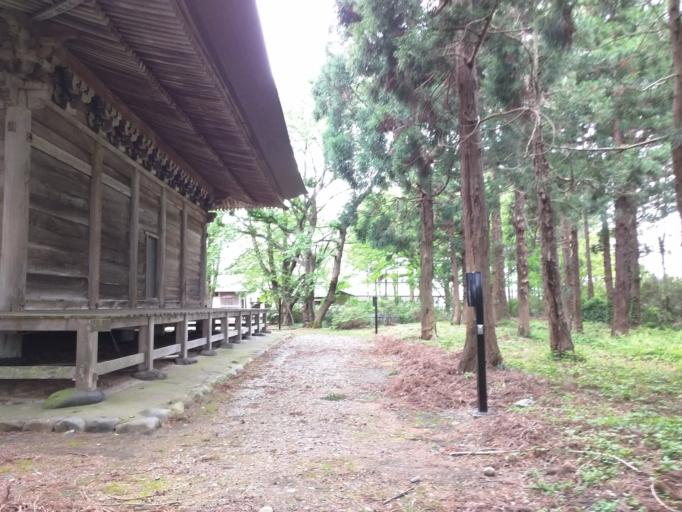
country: JP
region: Fukushima
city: Kitakata
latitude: 37.5638
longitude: 139.8699
